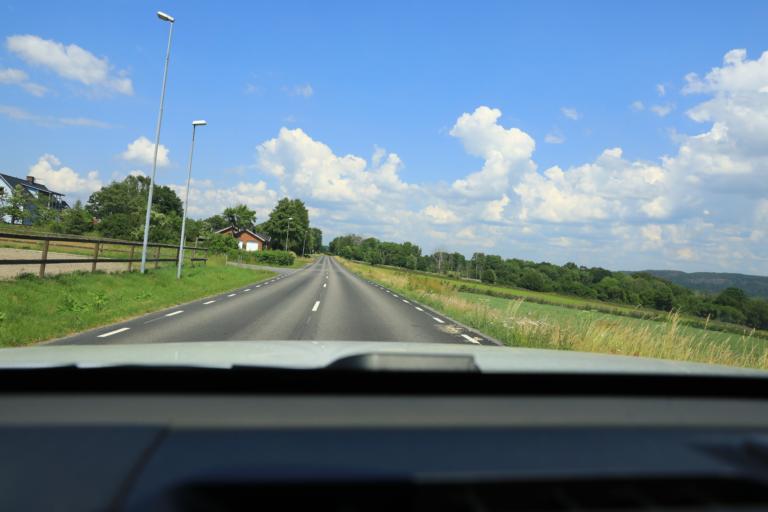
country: SE
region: Halland
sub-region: Varbergs Kommun
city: Veddige
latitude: 57.1987
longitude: 12.2915
